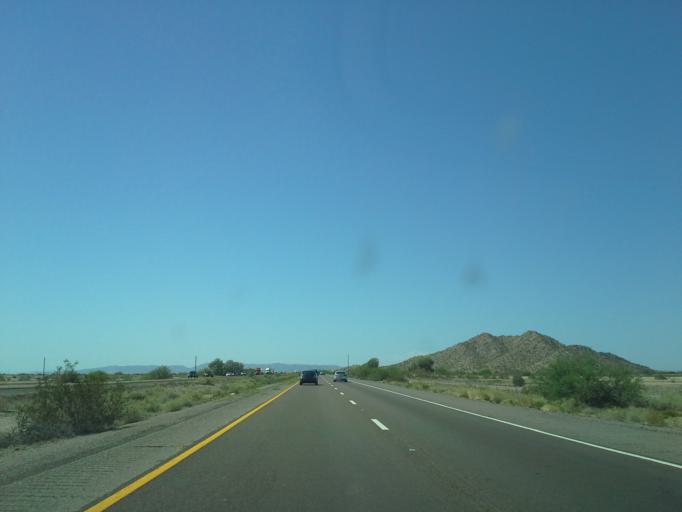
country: US
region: Arizona
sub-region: Pinal County
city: Casa Blanca
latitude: 33.1356
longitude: -111.8555
